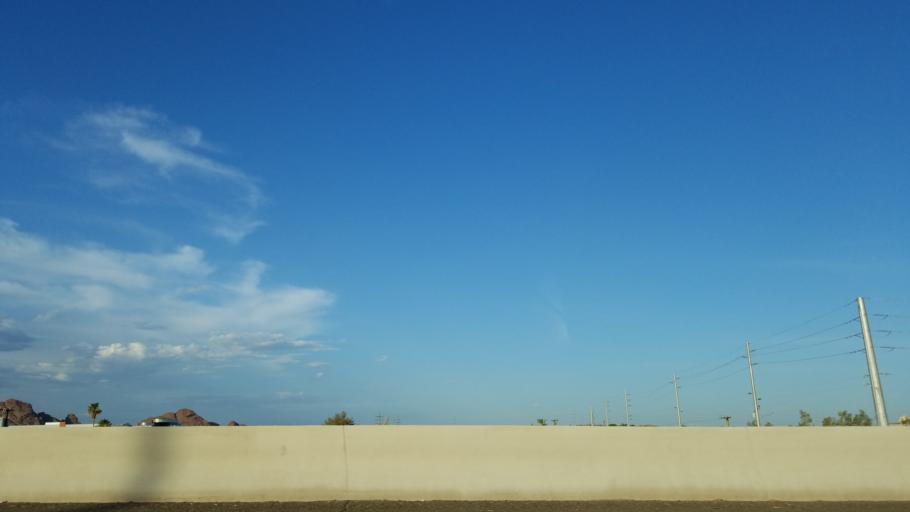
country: US
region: Arizona
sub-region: Maricopa County
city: Tempe Junction
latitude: 33.4524
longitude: -111.9820
